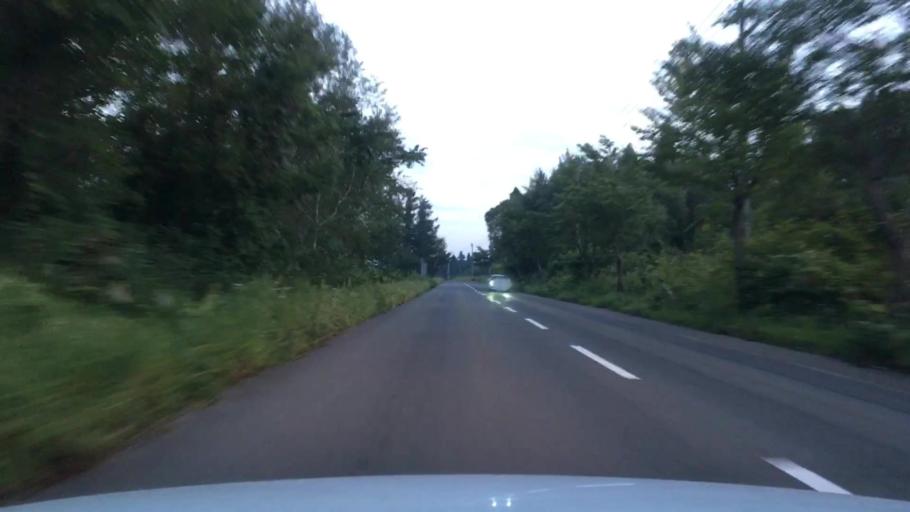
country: JP
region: Aomori
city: Shimokizukuri
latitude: 40.6831
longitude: 140.3703
